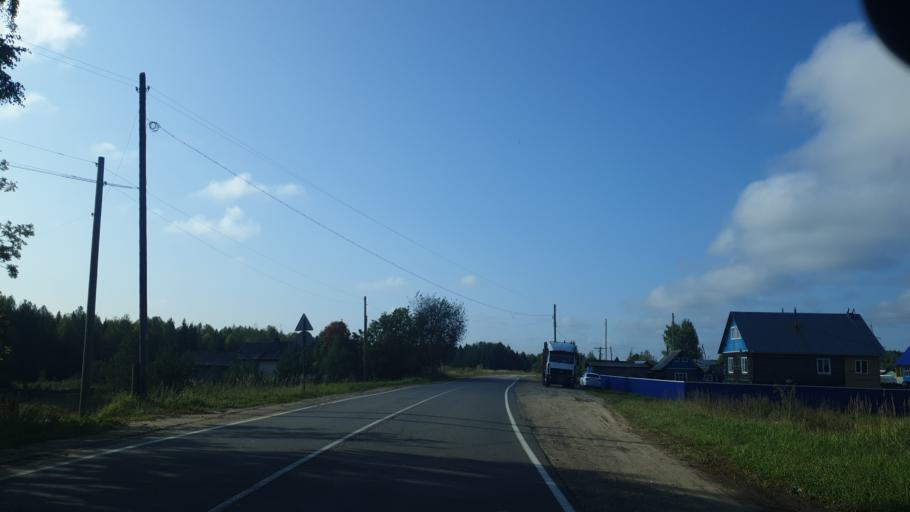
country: RU
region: Komi Republic
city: Vizinga
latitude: 60.9153
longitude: 50.2118
